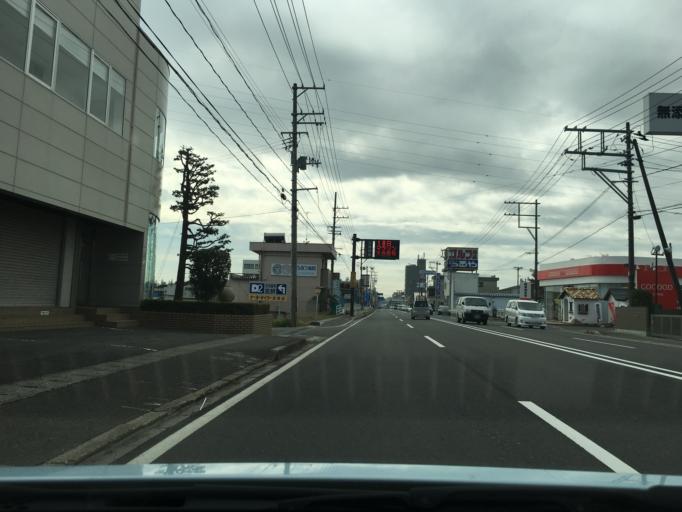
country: JP
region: Fukushima
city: Koriyama
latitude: 37.3651
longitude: 140.3694
